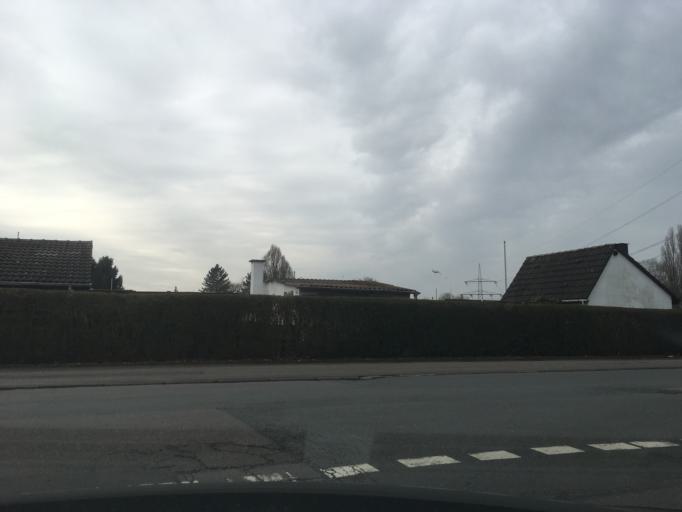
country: DE
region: North Rhine-Westphalia
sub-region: Regierungsbezirk Munster
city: Gladbeck
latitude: 51.5497
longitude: 7.0143
